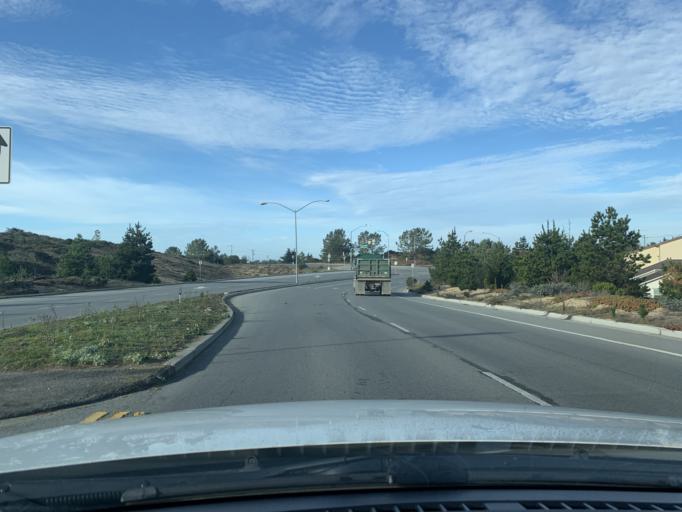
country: US
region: California
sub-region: Monterey County
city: Marina
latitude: 36.6618
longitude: -121.7899
